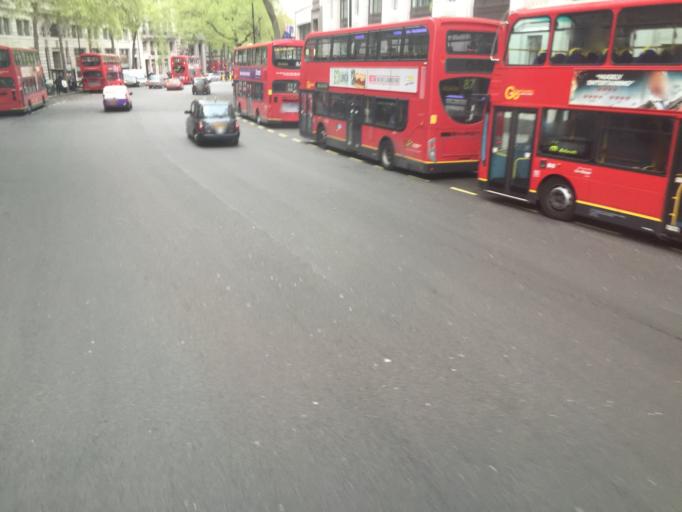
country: GB
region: England
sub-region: Greater London
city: London
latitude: 51.5132
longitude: -0.1172
